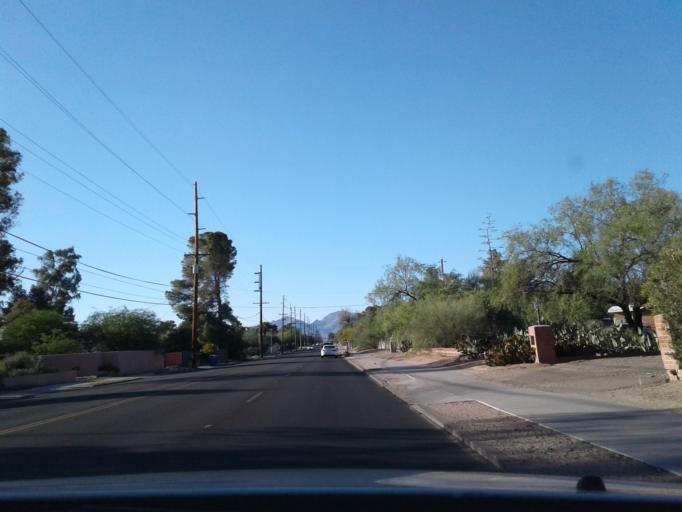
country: US
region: Arizona
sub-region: Pima County
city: Tucson
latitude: 32.2148
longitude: -110.9266
